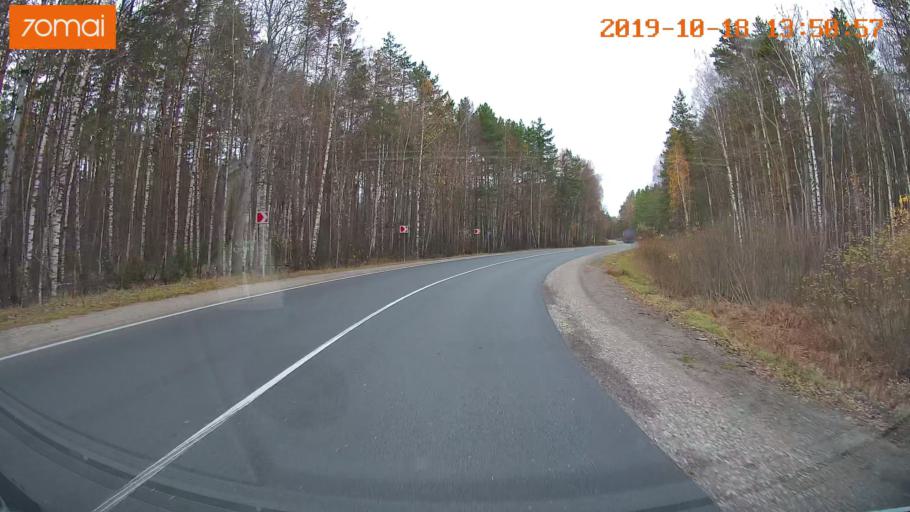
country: RU
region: Moskovskaya
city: Radovitskiy
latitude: 55.0120
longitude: 39.9648
